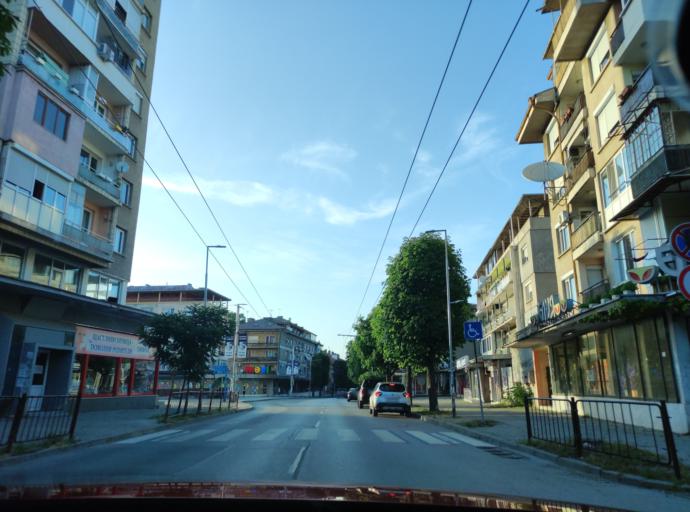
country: BG
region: Pleven
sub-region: Obshtina Pleven
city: Pleven
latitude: 43.4029
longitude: 24.6211
